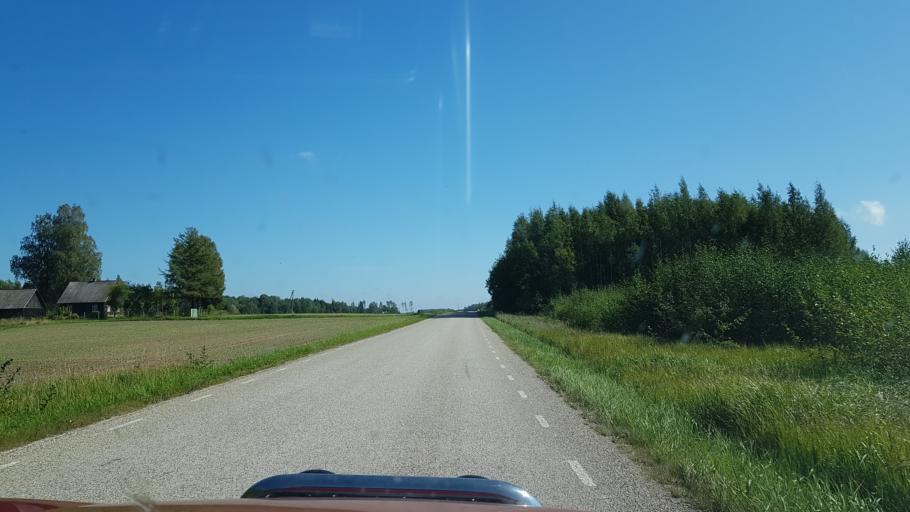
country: EE
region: Polvamaa
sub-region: Raepina vald
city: Rapina
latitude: 58.2336
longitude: 27.3199
